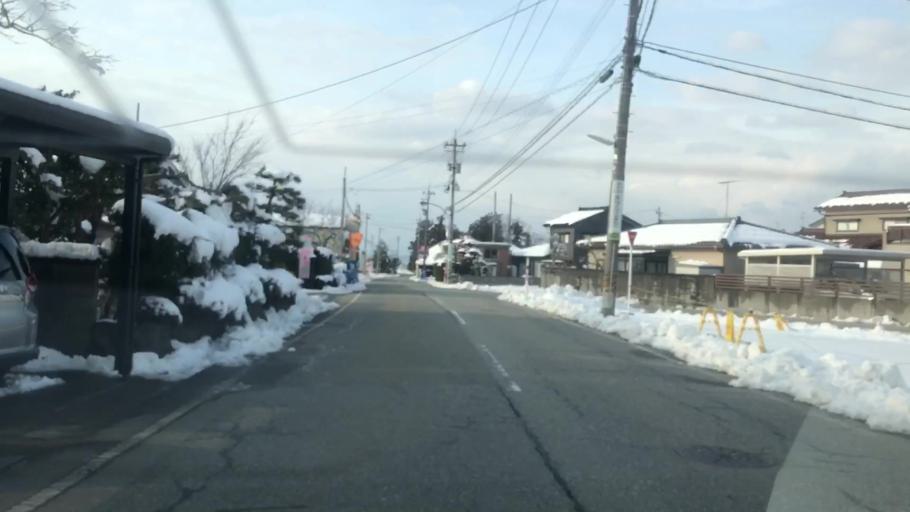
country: JP
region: Toyama
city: Toyama-shi
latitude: 36.6363
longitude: 137.2643
